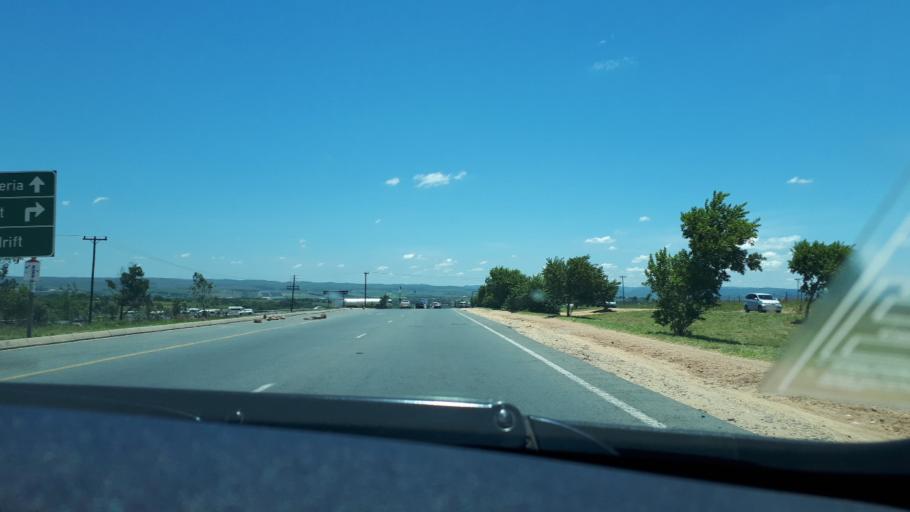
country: ZA
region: Gauteng
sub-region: West Rand District Municipality
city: Muldersdriseloop
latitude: -25.9985
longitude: 27.9263
